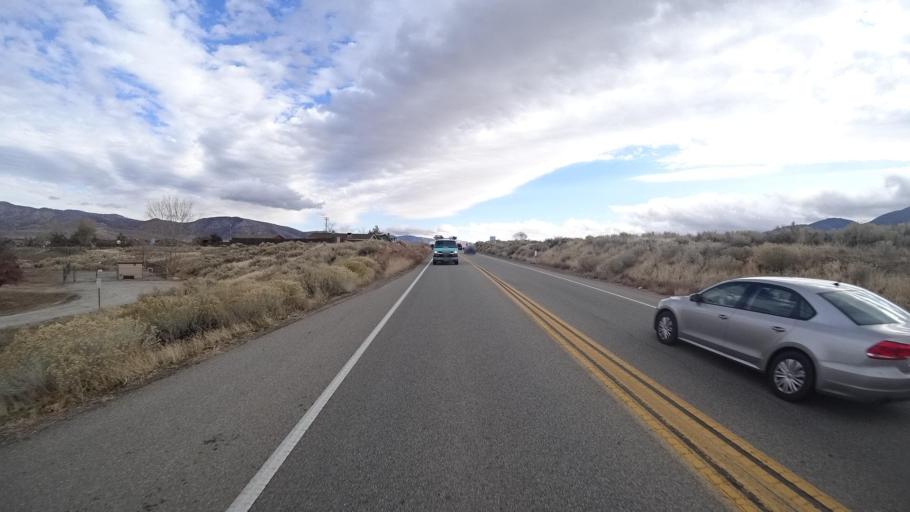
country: US
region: California
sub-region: Kern County
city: Golden Hills
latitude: 35.1243
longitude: -118.4831
